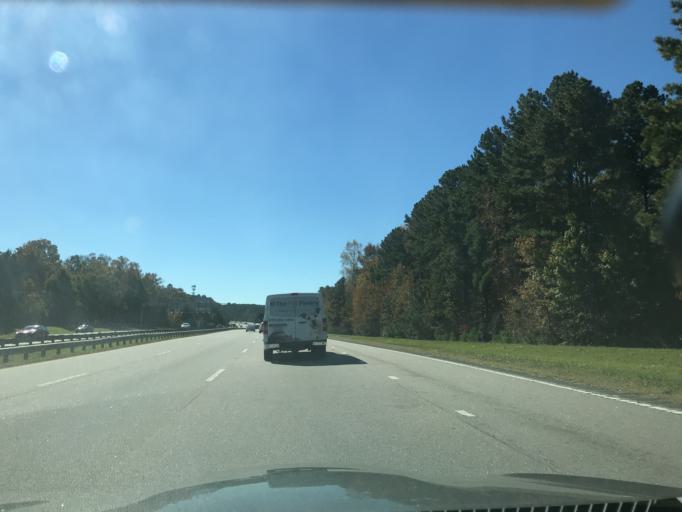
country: US
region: North Carolina
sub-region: Durham County
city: Durham
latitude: 36.0106
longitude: -78.9561
